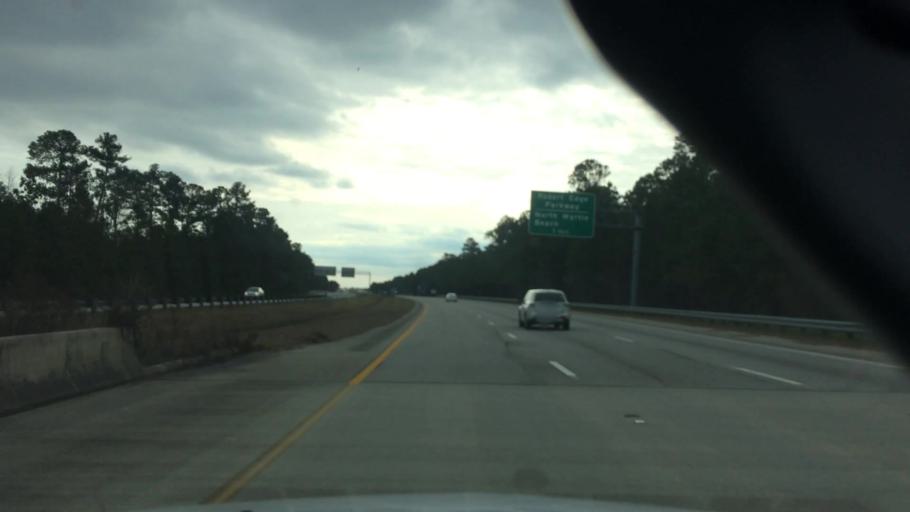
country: US
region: South Carolina
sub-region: Horry County
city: North Myrtle Beach
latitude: 33.8642
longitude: -78.6943
